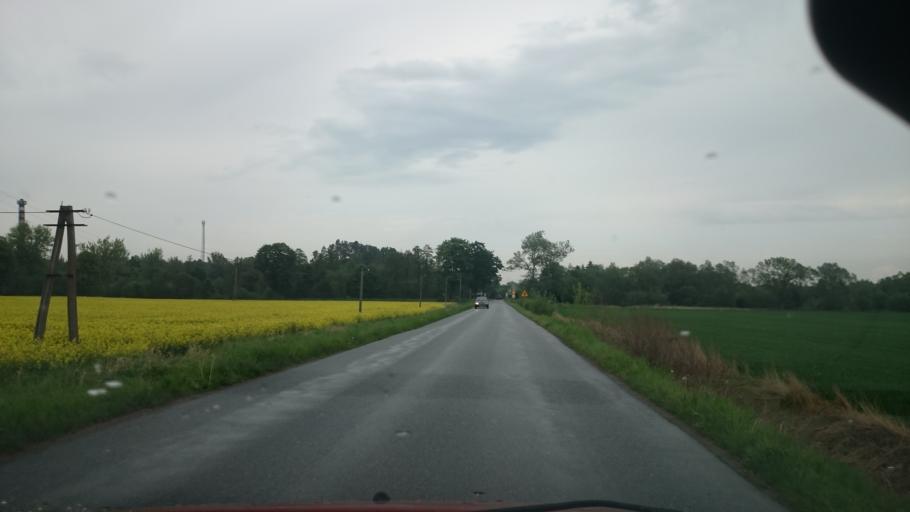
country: PL
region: Lower Silesian Voivodeship
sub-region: Powiat klodzki
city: Klodzko
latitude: 50.4126
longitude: 16.6389
